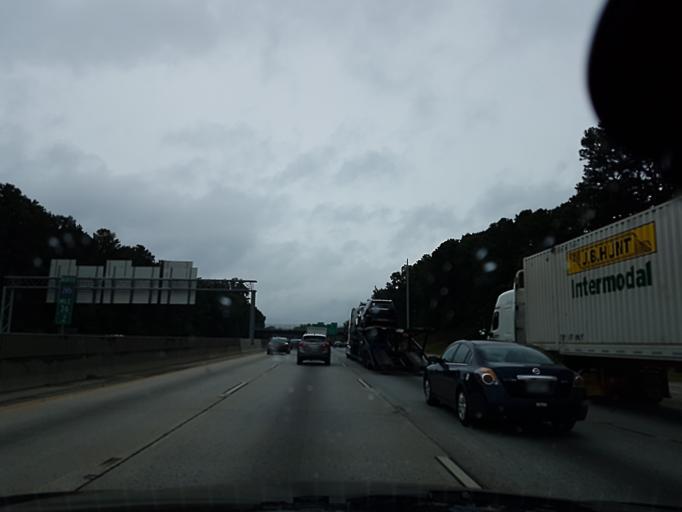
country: US
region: Georgia
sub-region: DeKalb County
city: Tucker
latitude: 33.8489
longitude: -84.2468
